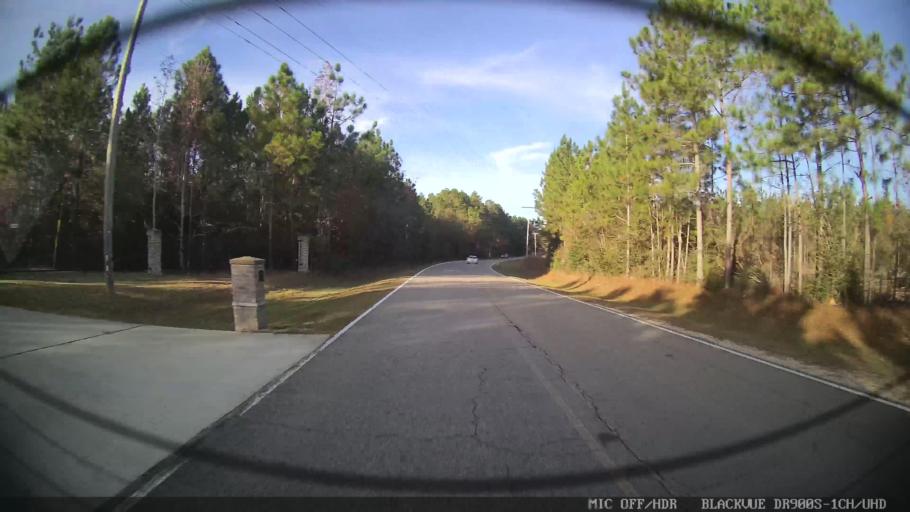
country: US
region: Mississippi
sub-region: Lamar County
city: Purvis
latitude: 31.1738
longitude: -89.2953
